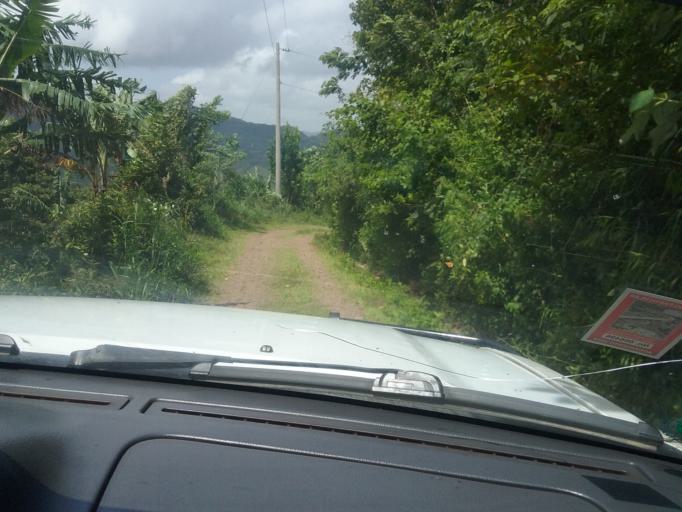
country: NI
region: Matagalpa
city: Matagalpa
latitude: 12.8663
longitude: -85.9109
